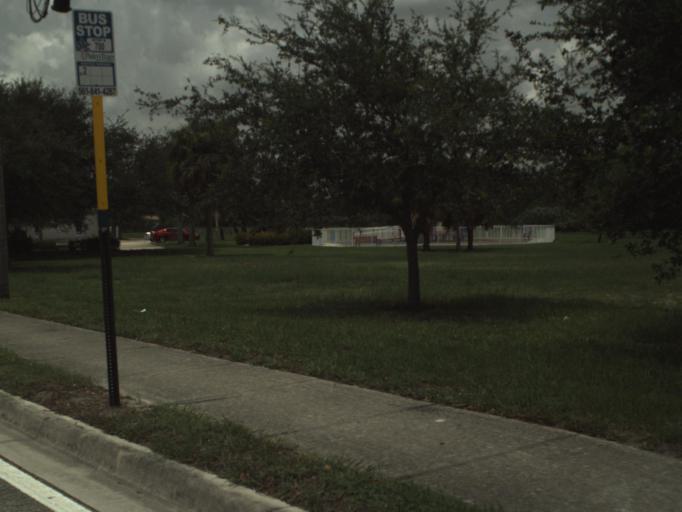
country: US
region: Florida
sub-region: Palm Beach County
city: Delray Beach
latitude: 26.4751
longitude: -80.0912
